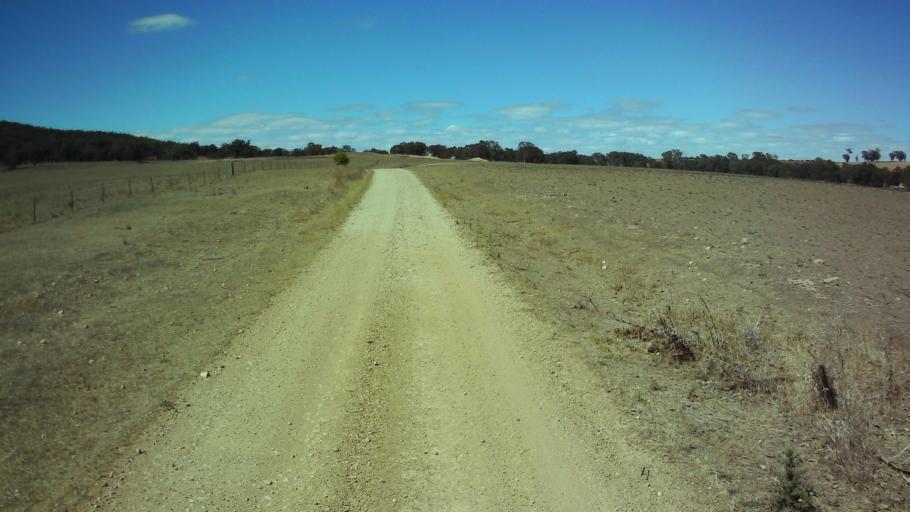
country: AU
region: New South Wales
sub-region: Weddin
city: Grenfell
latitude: -34.0394
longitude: 148.4316
